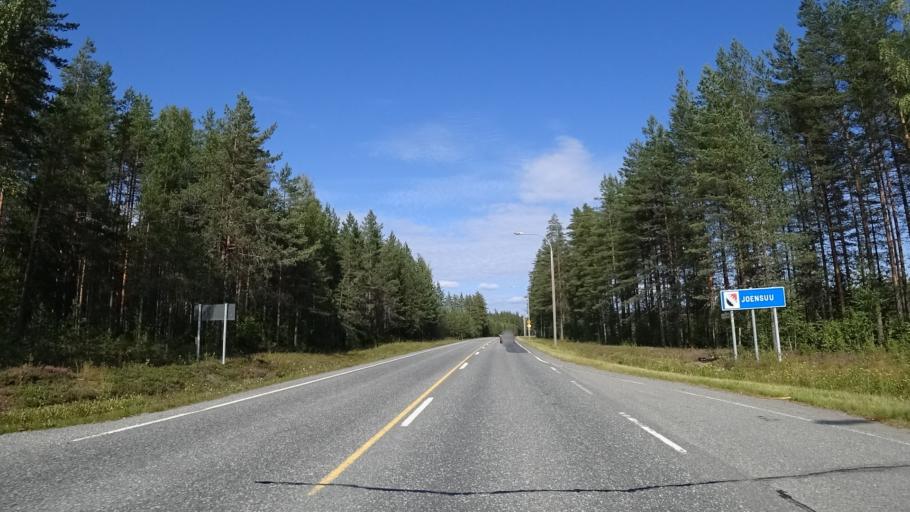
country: FI
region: North Karelia
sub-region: Joensuu
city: Eno
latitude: 62.7719
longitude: 30.0504
